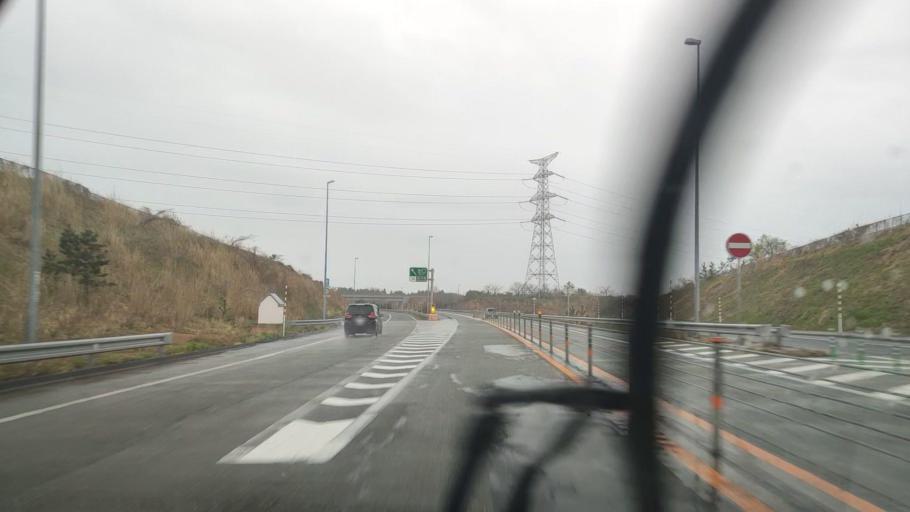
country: JP
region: Akita
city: Noshiromachi
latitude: 40.1558
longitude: 140.0244
